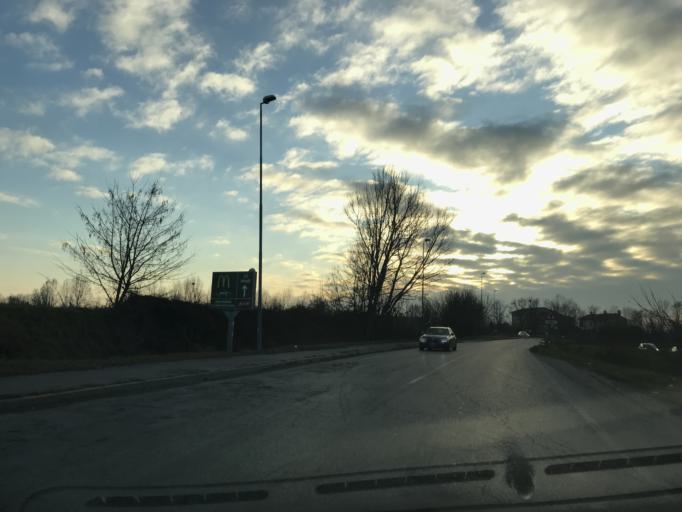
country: IT
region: Lombardy
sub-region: Provincia di Lodi
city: Muzza di Cornegliano Laudense
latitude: 45.2935
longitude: 9.4789
